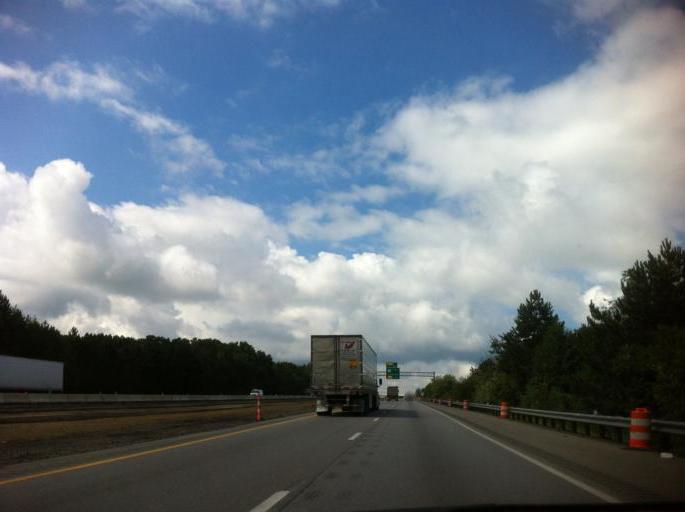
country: US
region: Ohio
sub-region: Trumbull County
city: McDonald
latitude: 41.1389
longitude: -80.7274
